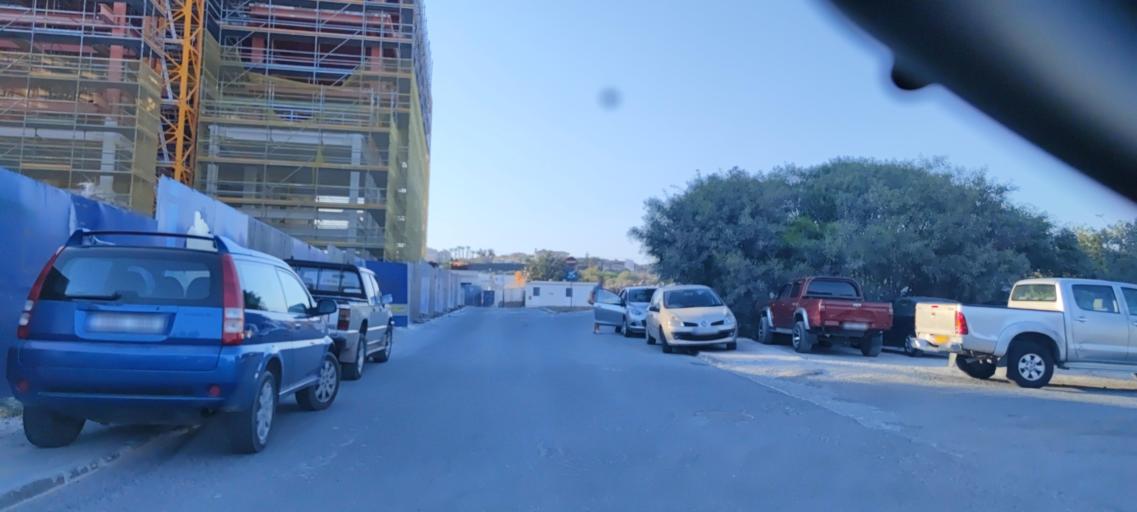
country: CY
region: Limassol
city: Mouttagiaka
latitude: 34.7068
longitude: 33.1177
